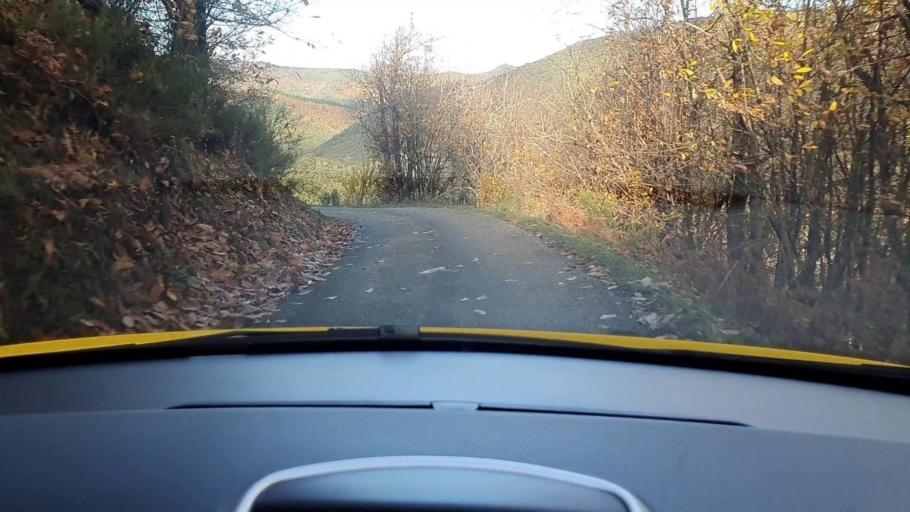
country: FR
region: Languedoc-Roussillon
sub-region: Departement du Gard
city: Valleraugue
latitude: 44.0992
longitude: 3.7380
